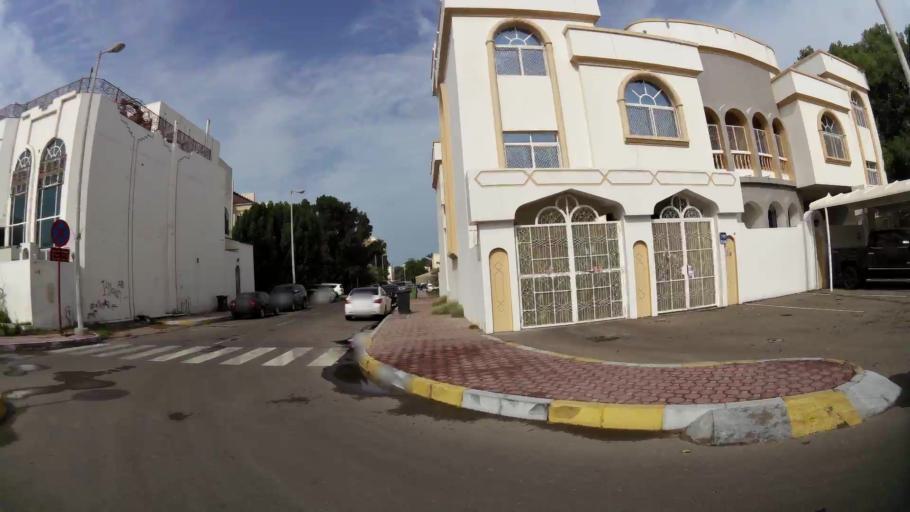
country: AE
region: Abu Dhabi
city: Abu Dhabi
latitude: 24.4404
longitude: 54.4171
